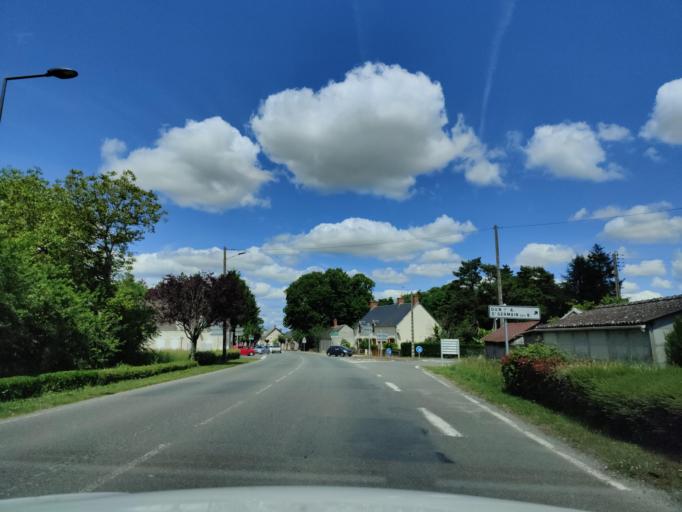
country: FR
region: Centre
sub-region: Departement du Cher
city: Levet
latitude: 46.9217
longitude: 2.4107
